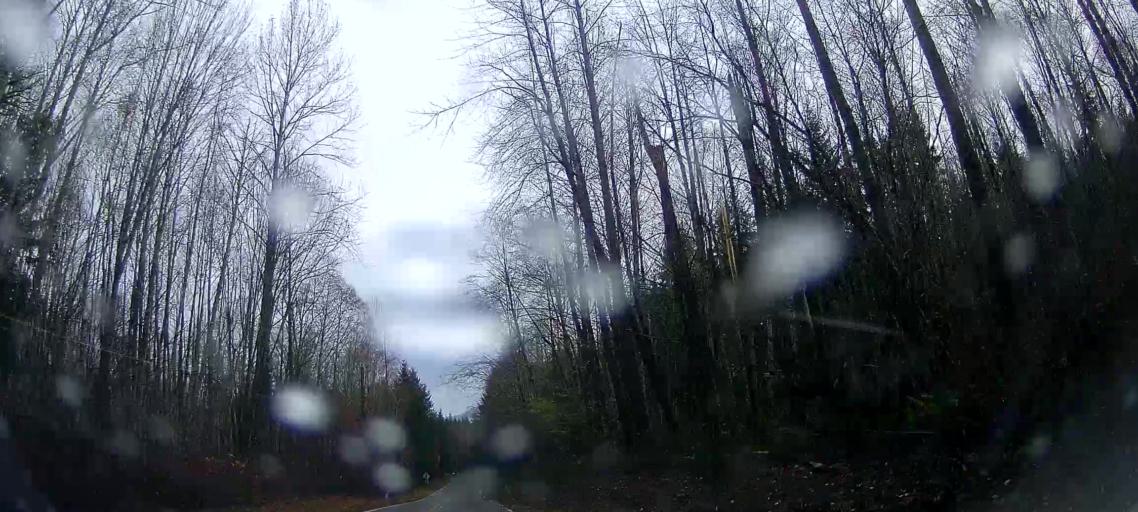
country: US
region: Washington
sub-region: Skagit County
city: Clear Lake
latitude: 48.4767
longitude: -122.1524
